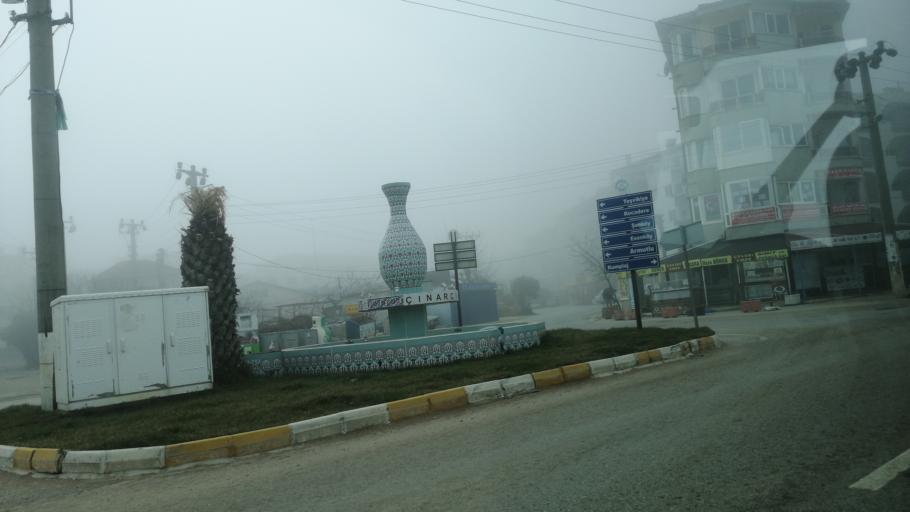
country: TR
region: Yalova
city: Cinarcik
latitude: 40.6450
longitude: 29.0880
